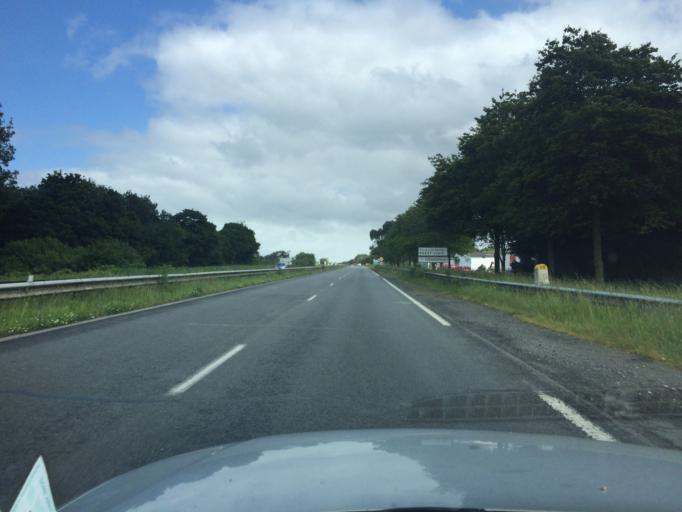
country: FR
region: Brittany
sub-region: Departement du Finistere
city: Gouesnou
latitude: 48.4332
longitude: -4.4604
